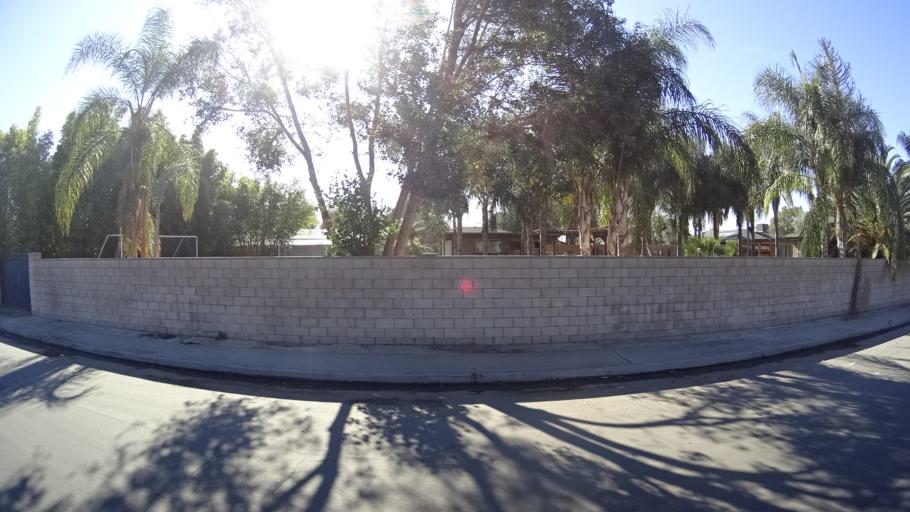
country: US
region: California
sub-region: Kern County
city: Greenacres
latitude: 35.3761
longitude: -119.1220
